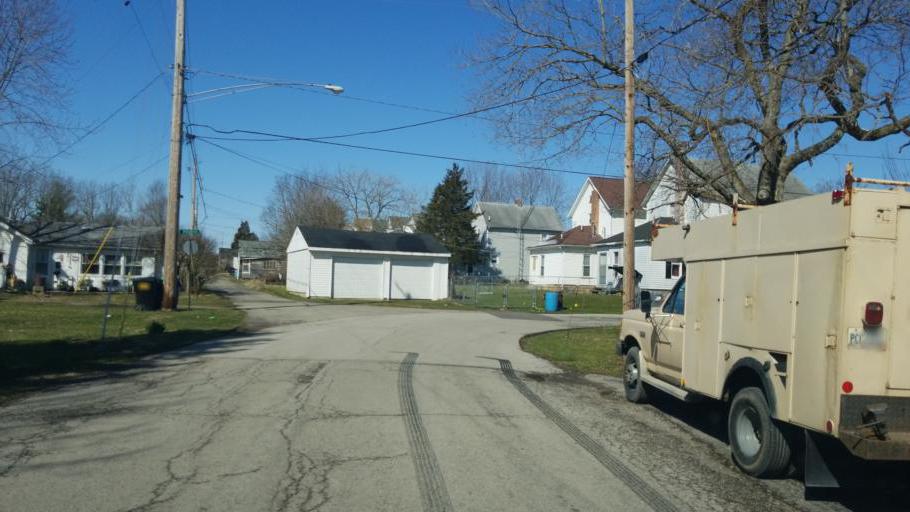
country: US
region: Ohio
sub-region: Highland County
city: Greenfield
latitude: 39.3428
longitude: -83.3830
